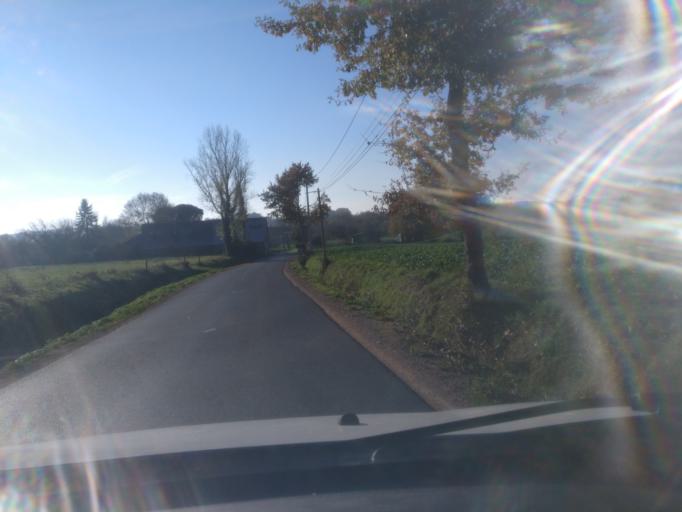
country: FR
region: Brittany
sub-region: Departement d'Ille-et-Vilaine
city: Guichen
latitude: 48.0097
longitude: -1.7914
